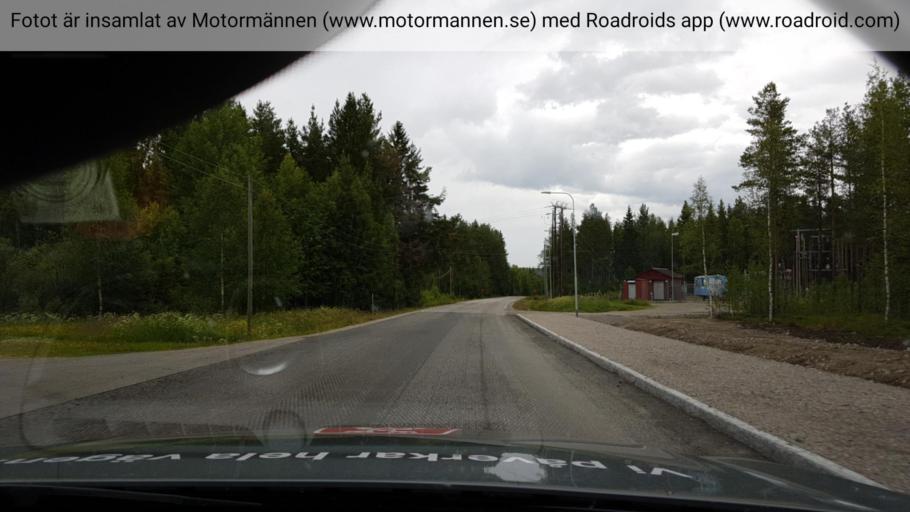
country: SE
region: Jaemtland
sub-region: Bergs Kommun
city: Hoverberg
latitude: 62.4837
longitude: 14.5410
